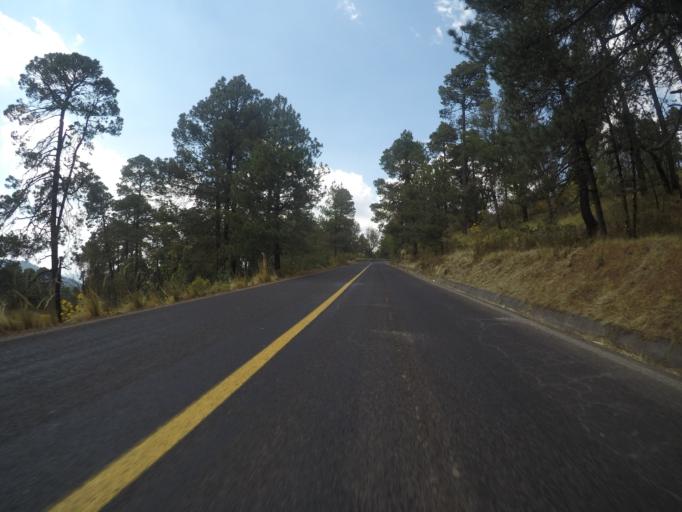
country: MX
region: Mexico
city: Cerro La Calera
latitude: 19.1346
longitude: -99.8150
